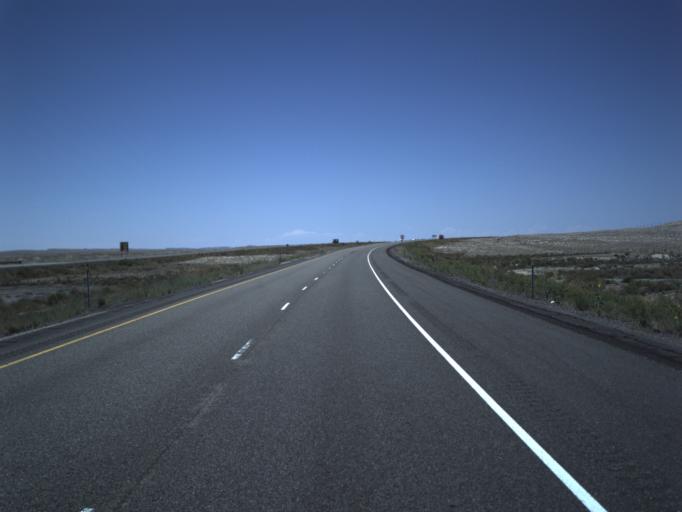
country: US
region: Utah
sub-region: Grand County
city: Moab
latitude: 38.9335
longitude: -109.4245
